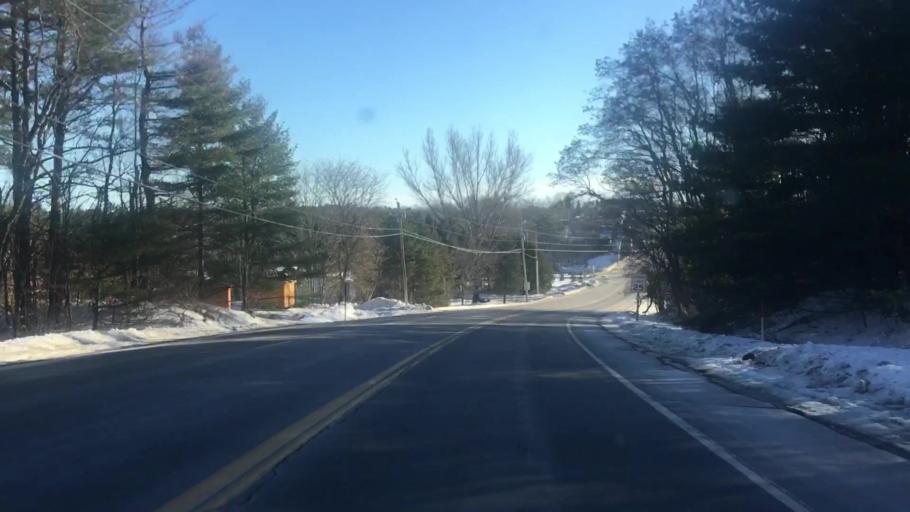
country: US
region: Maine
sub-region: Somerset County
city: Norridgewock
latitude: 44.7199
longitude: -69.7979
